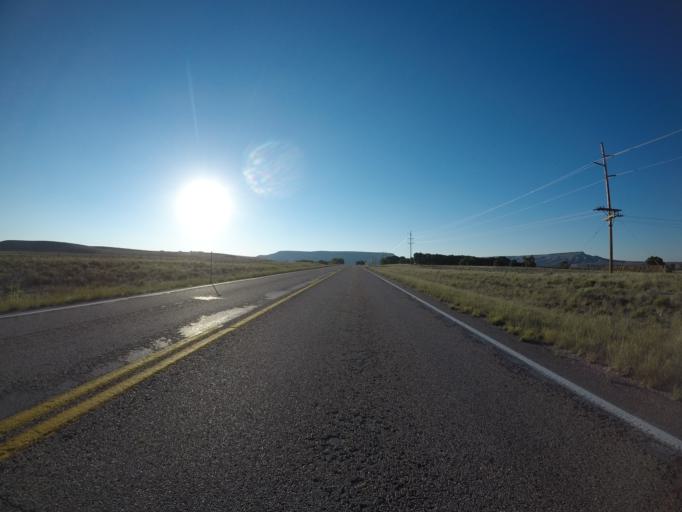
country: US
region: Wyoming
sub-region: Sublette County
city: Marbleton
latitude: 42.5705
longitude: -109.9624
